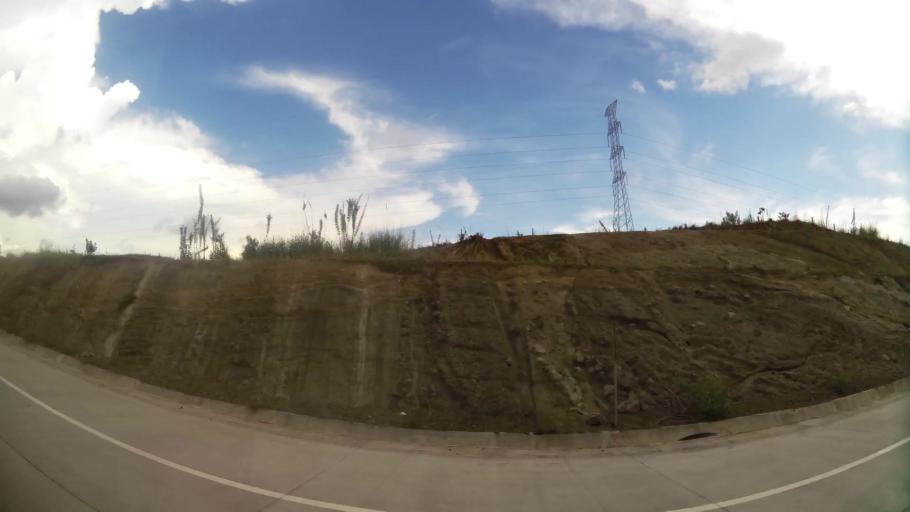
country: PA
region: Panama
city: Tocumen
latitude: 9.1096
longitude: -79.4065
